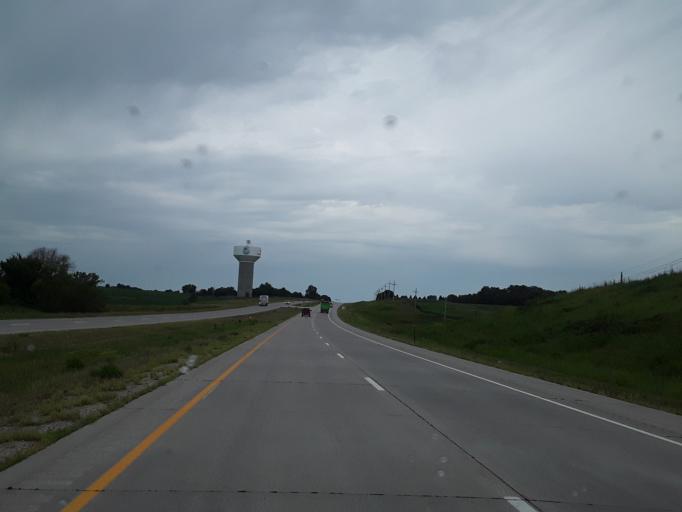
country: US
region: Nebraska
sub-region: Washington County
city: Blair
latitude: 41.4950
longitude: -96.1481
